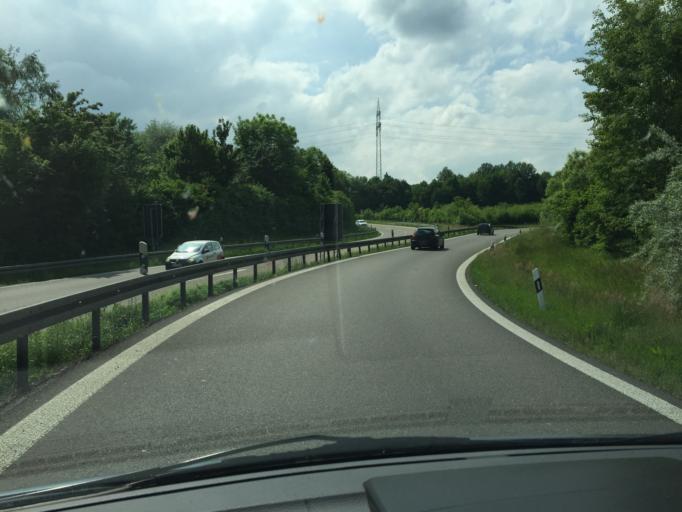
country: DE
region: Baden-Wuerttemberg
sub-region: Regierungsbezirk Stuttgart
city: Unterensingen
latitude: 48.6693
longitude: 9.3569
